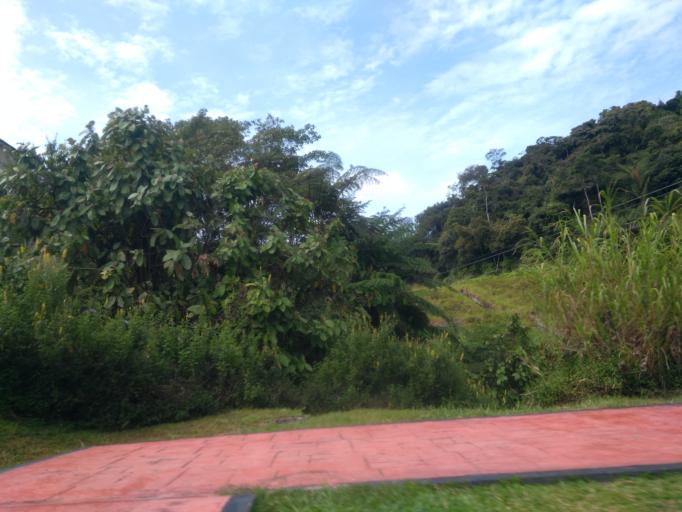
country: MY
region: Pahang
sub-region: Cameron Highlands
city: Tanah Rata
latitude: 4.4684
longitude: 101.3721
